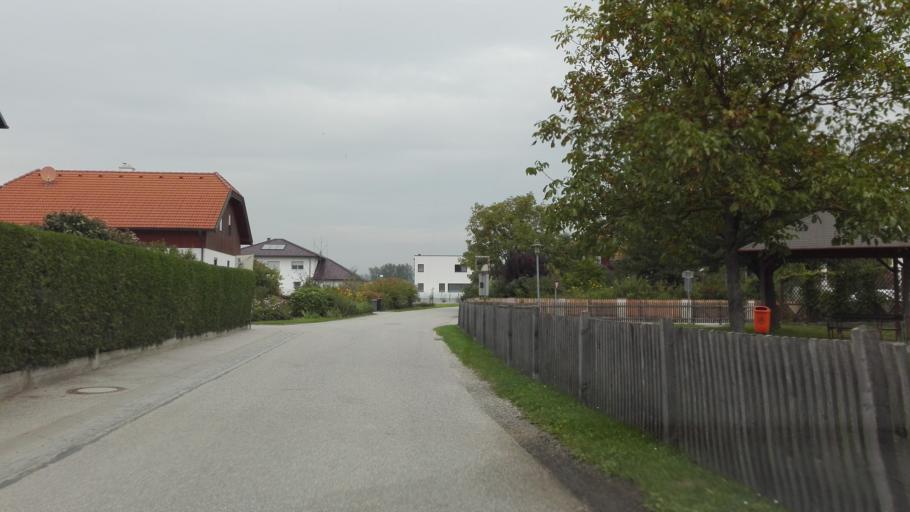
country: AT
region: Upper Austria
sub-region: Politischer Bezirk Urfahr-Umgebung
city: Feldkirchen an der Donau
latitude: 48.3195
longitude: 14.0213
